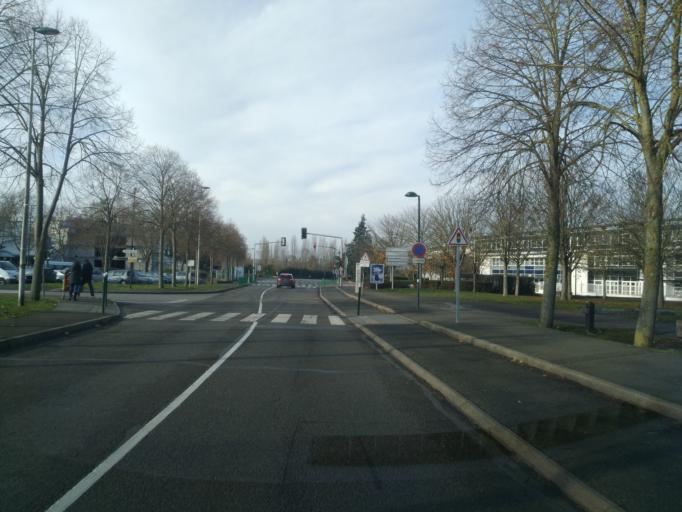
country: FR
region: Ile-de-France
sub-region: Departement des Yvelines
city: Plaisir
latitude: 48.8239
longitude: 1.9548
